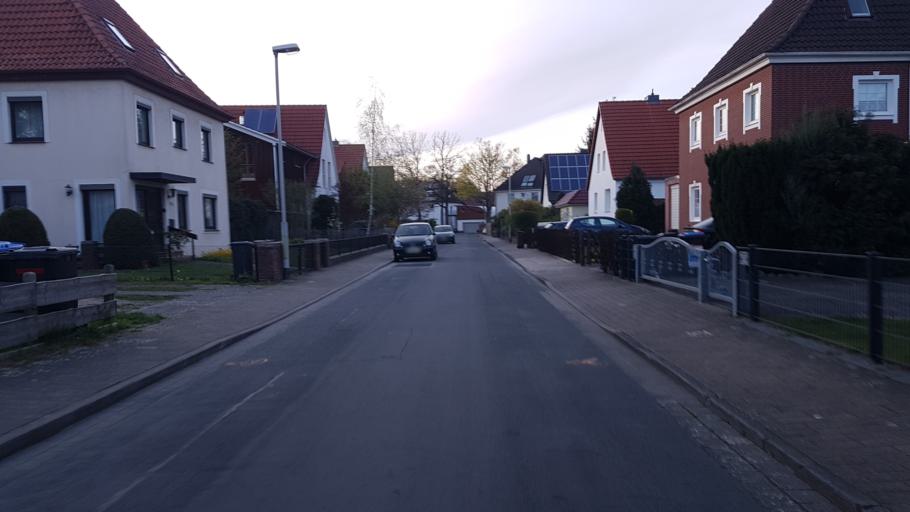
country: DE
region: Lower Saxony
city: Isernhagen Farster Bauerschaft
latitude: 52.4225
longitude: 9.8076
